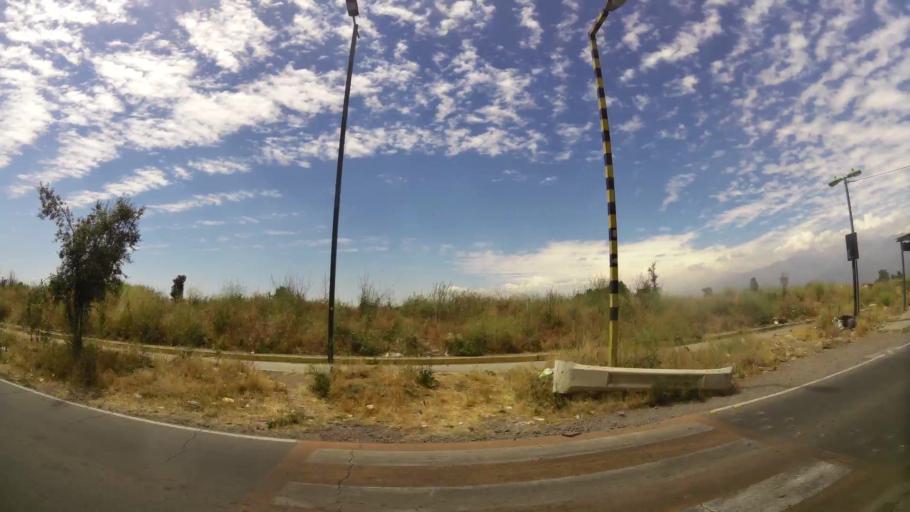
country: CL
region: Santiago Metropolitan
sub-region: Provincia de Santiago
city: La Pintana
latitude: -33.5749
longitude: -70.6518
